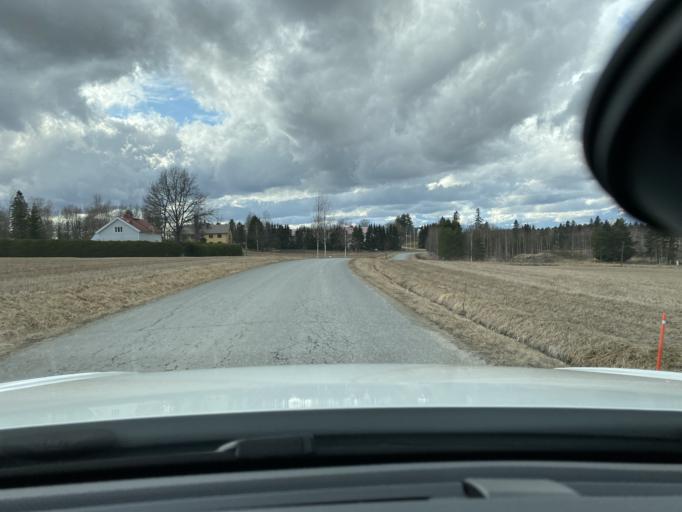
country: FI
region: Pirkanmaa
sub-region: Lounais-Pirkanmaa
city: Punkalaidun
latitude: 61.1187
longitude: 23.0564
